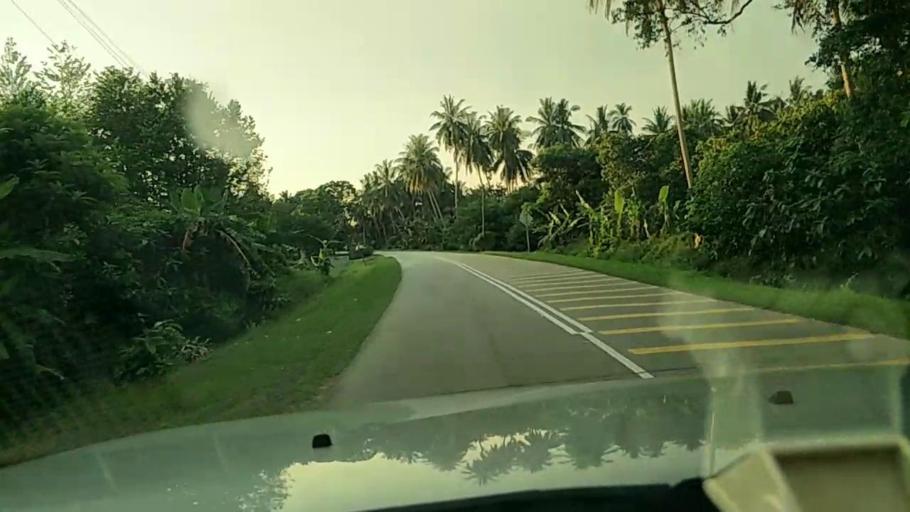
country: MY
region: Selangor
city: Kuala Selangor
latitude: 3.3036
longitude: 101.2960
